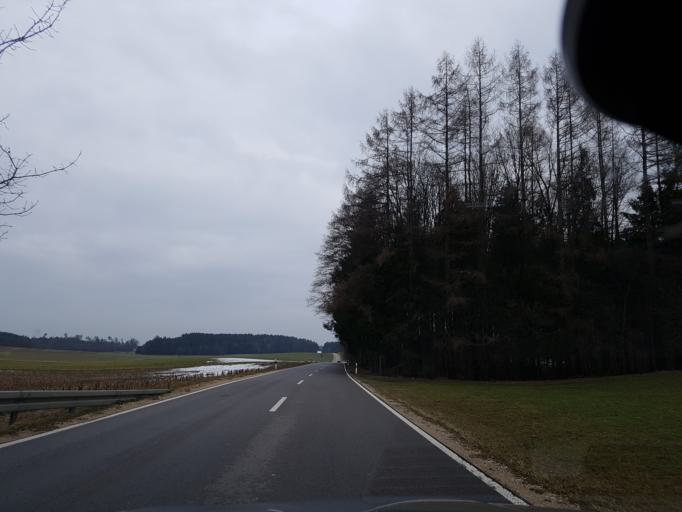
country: DE
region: Bavaria
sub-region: Upper Bavaria
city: Aying
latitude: 47.9417
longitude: 11.8107
